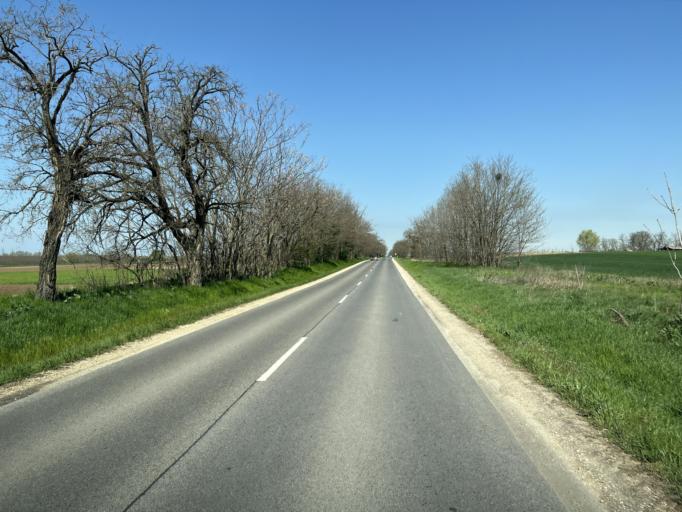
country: HU
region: Pest
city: Ocsa
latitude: 47.3082
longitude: 19.2122
